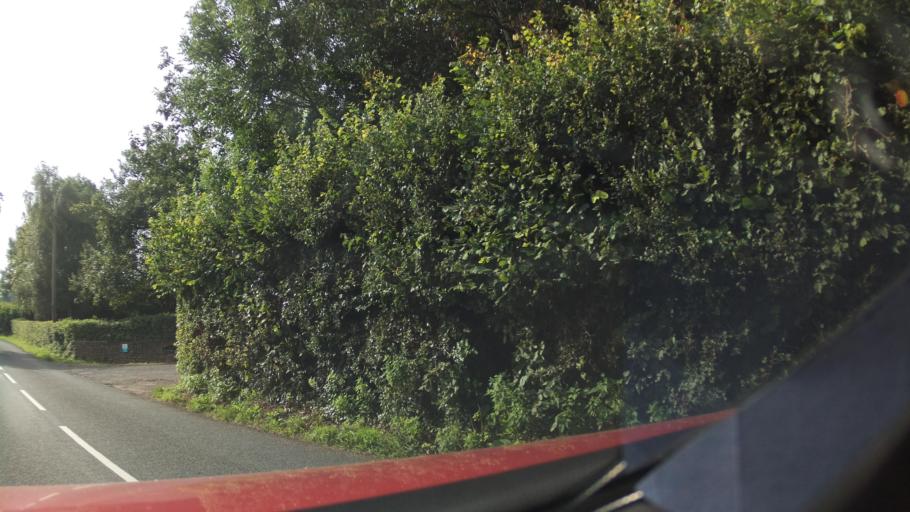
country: GB
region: England
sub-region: Bath and North East Somerset
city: East Harptree
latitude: 51.3078
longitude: -2.6277
